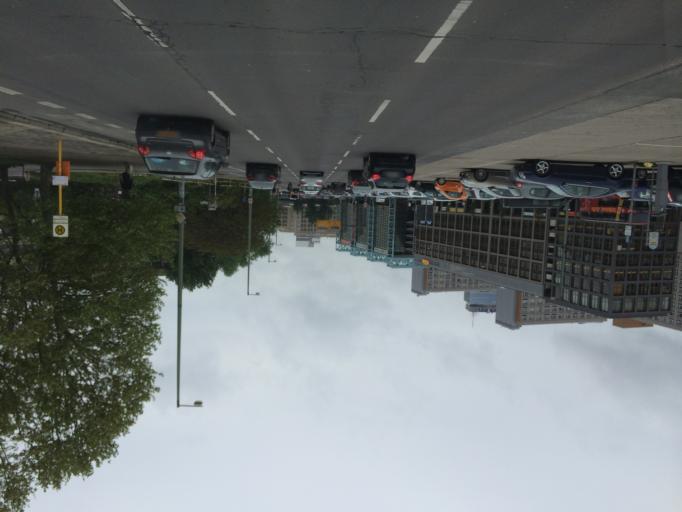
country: DE
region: Berlin
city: Mitte
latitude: 52.5171
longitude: 13.4095
